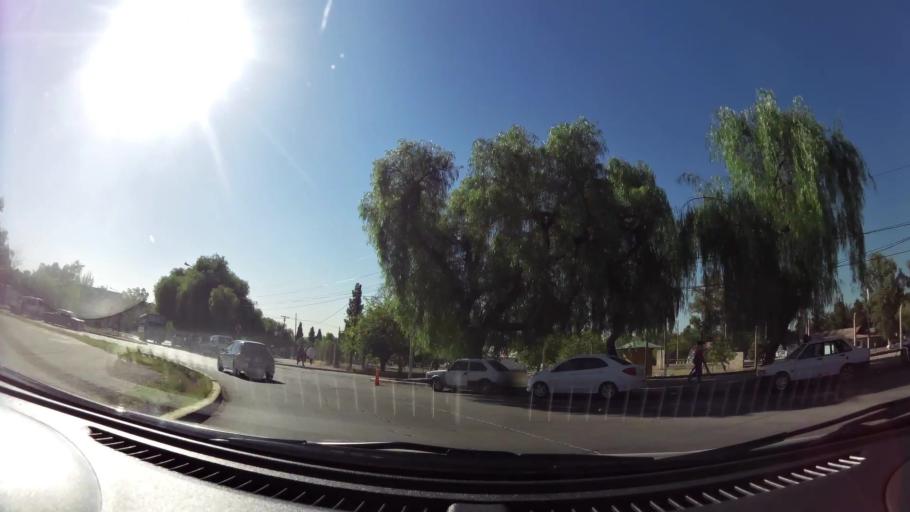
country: AR
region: Mendoza
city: Las Heras
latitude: -32.8723
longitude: -68.8634
